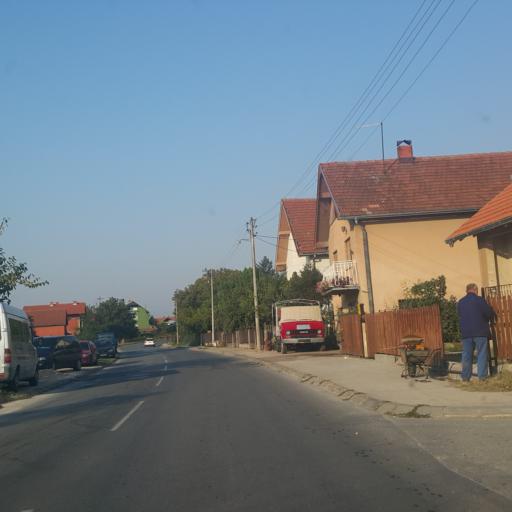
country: RS
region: Central Serbia
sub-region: Zajecarski Okrug
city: Zajecar
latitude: 43.9129
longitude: 22.2713
